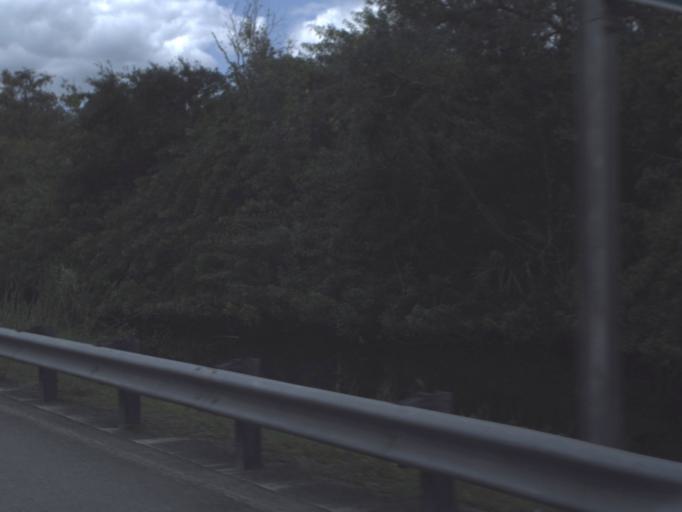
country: US
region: Florida
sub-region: Collier County
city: Lely Resort
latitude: 25.9956
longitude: -81.5939
